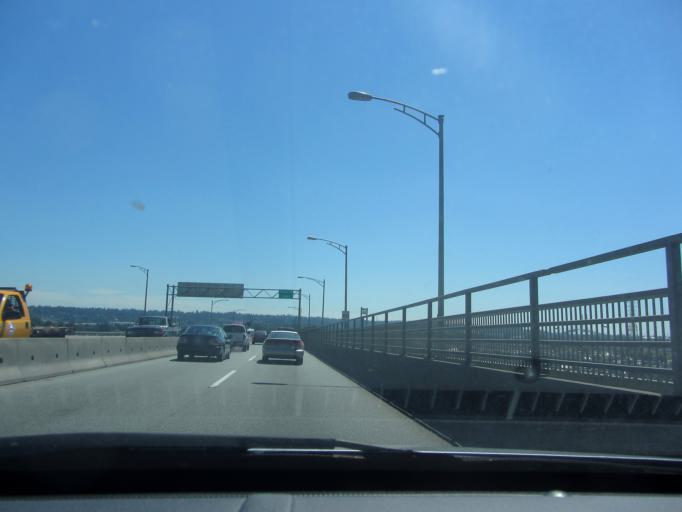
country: CA
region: British Columbia
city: New Westminster
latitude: 49.1981
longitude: -122.9491
